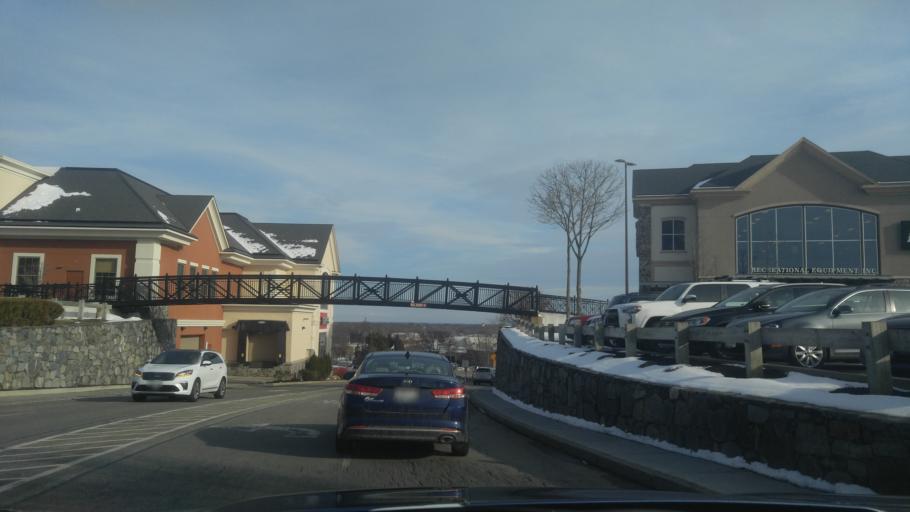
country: US
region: Rhode Island
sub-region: Providence County
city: Cranston
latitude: 41.7559
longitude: -71.4598
